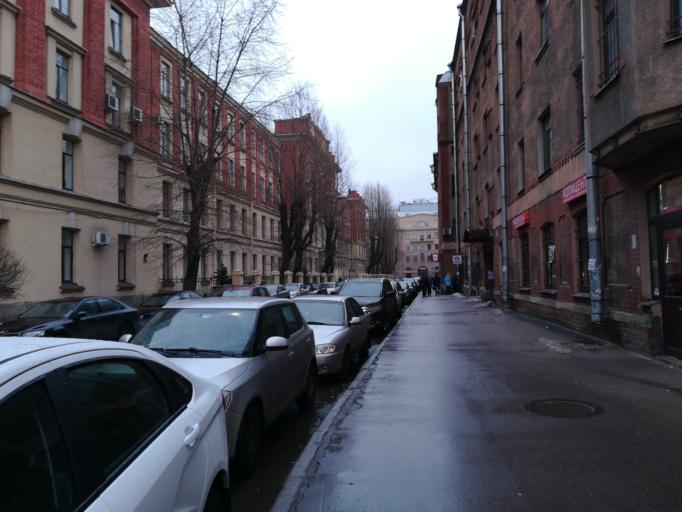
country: RU
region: St.-Petersburg
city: Petrogradka
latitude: 59.9583
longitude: 30.3295
